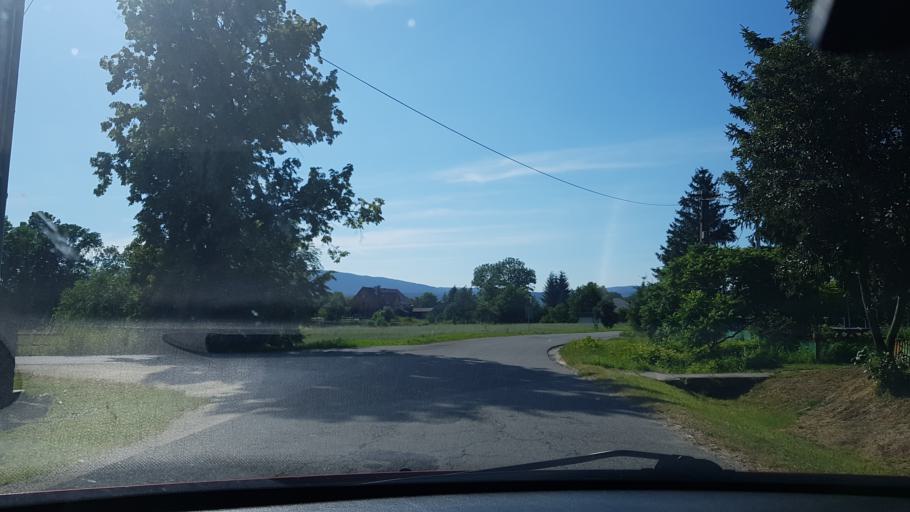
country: PL
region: Lower Silesian Voivodeship
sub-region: Powiat klodzki
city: Bystrzyca Klodzka
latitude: 50.2431
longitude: 16.7105
